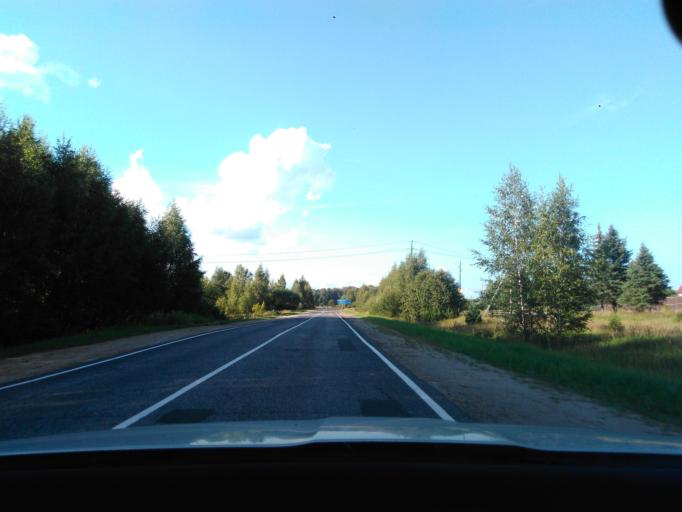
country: RU
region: Tverskaya
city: Zavidovo
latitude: 56.6057
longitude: 36.5415
